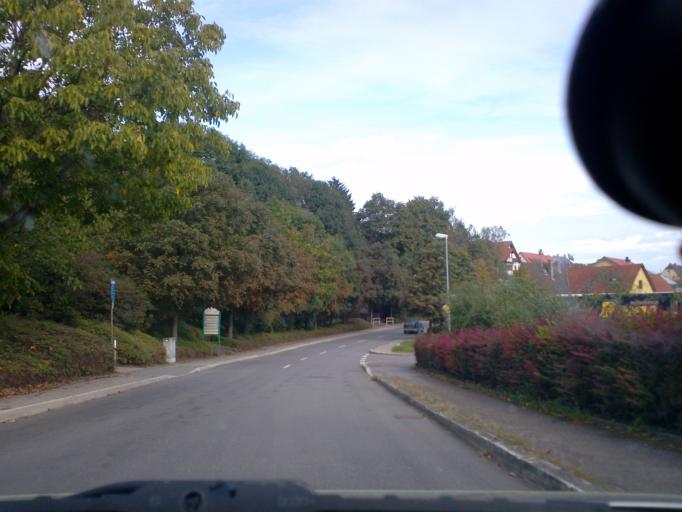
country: DE
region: Baden-Wuerttemberg
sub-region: Regierungsbezirk Stuttgart
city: Gemmingen
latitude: 49.1471
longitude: 8.9624
